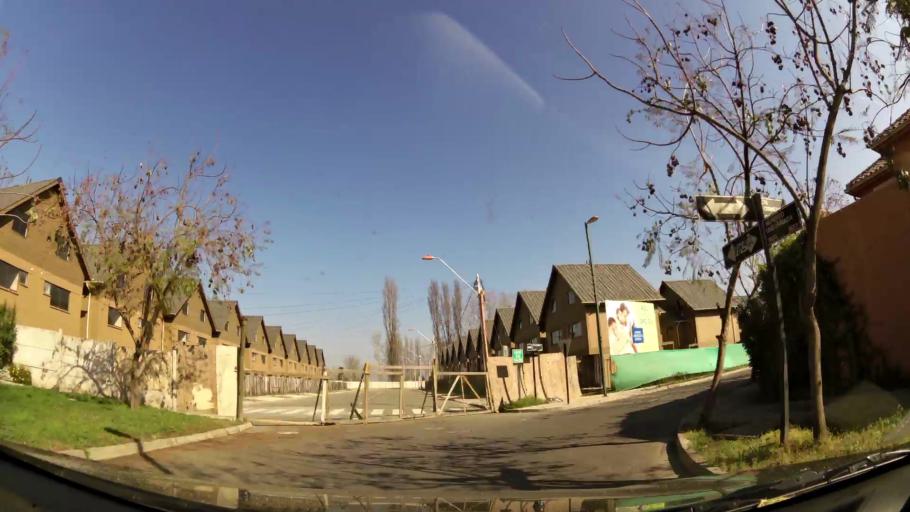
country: CL
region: Santiago Metropolitan
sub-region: Provincia de Chacabuco
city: Chicureo Abajo
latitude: -33.3567
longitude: -70.6786
